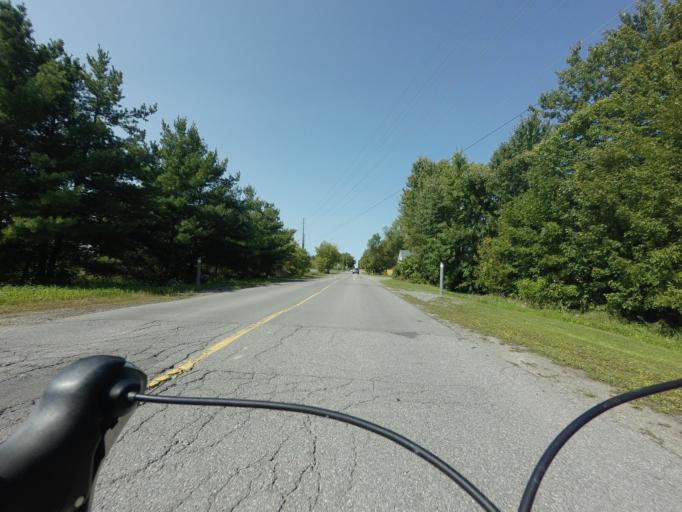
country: CA
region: Ontario
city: Arnprior
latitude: 45.4940
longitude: -76.1415
